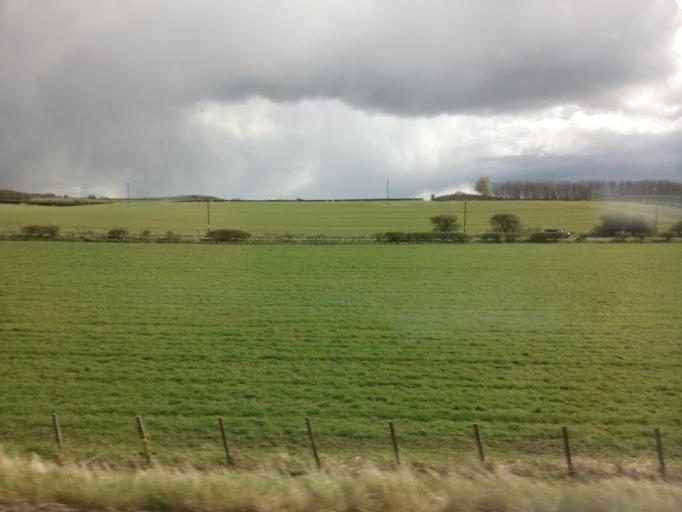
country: GB
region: Scotland
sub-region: East Lothian
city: Gullane
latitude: 55.9880
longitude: -2.8426
